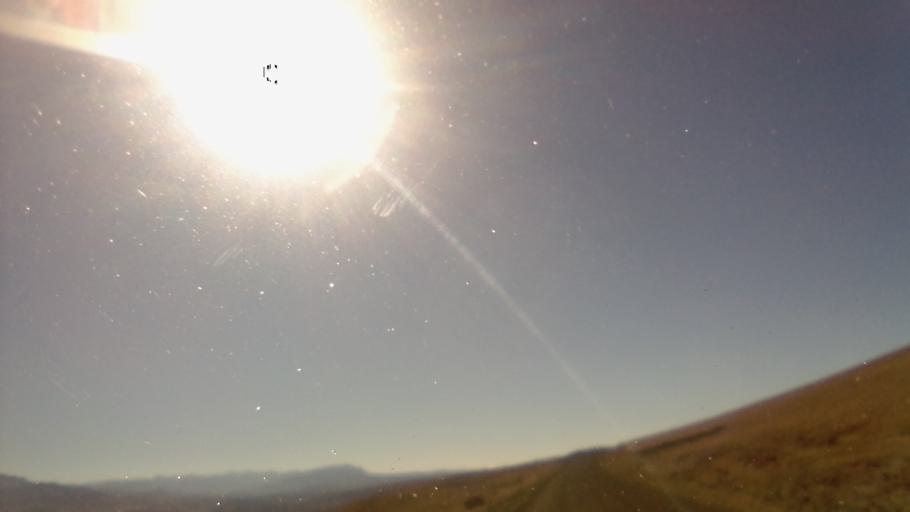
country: LS
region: Qacha's Nek
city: Qacha's Nek
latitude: -30.0371
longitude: 28.9467
